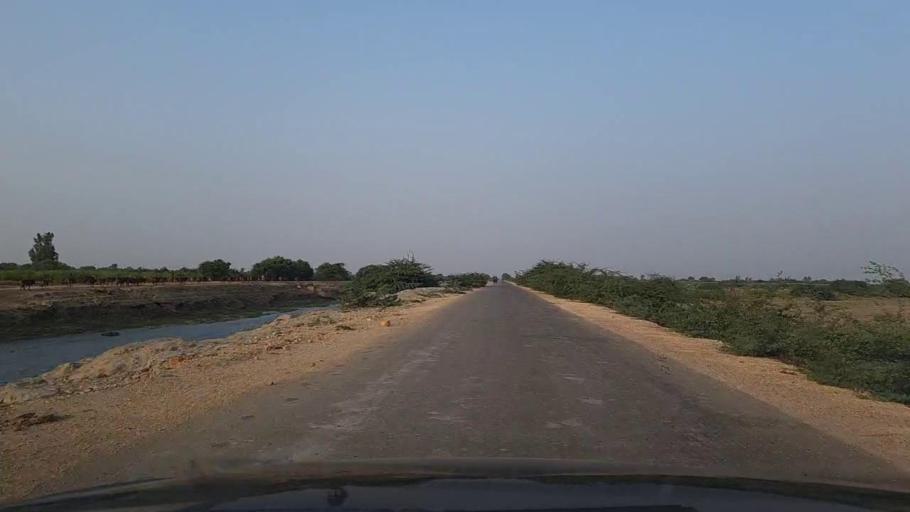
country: PK
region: Sindh
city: Mirpur Sakro
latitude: 24.4891
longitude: 67.8087
